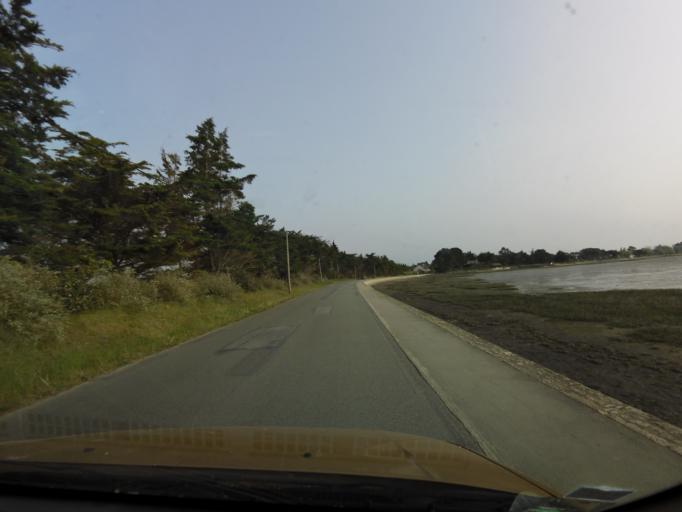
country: FR
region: Brittany
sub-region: Departement du Morbihan
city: Sene
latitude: 47.5817
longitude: -2.7152
